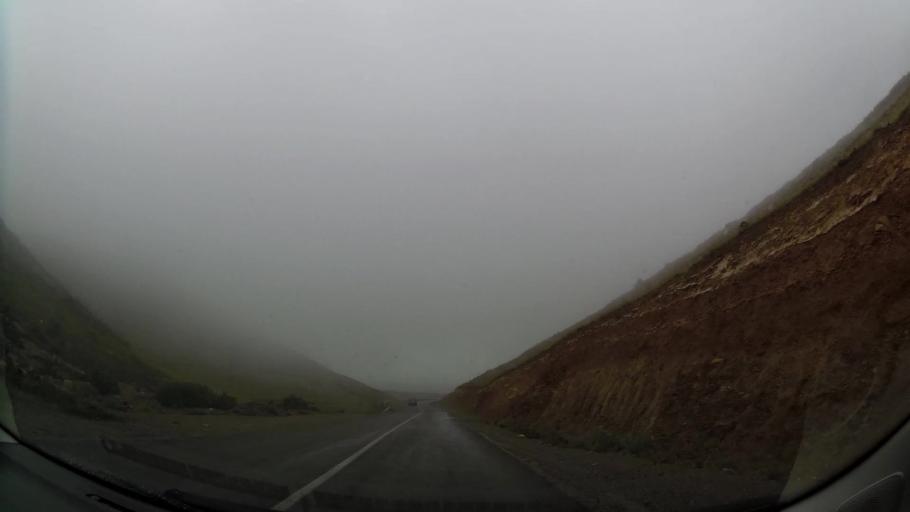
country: MA
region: Oriental
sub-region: Nador
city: Boudinar
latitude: 35.1079
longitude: -3.5671
